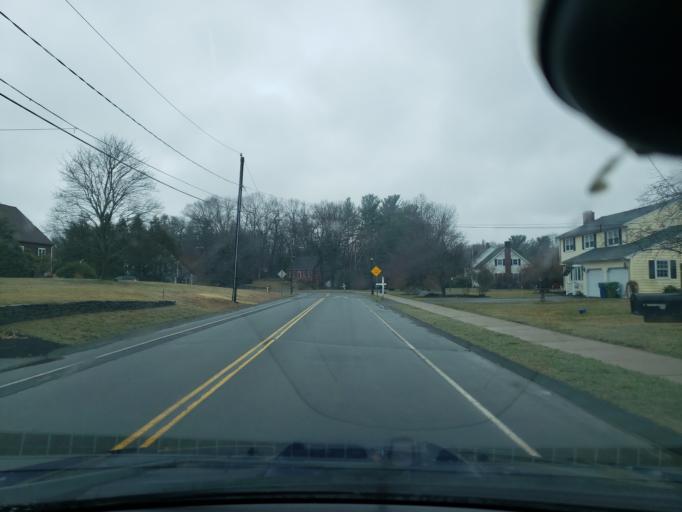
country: US
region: Connecticut
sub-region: Hartford County
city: Tariffville
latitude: 41.8950
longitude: -72.7004
